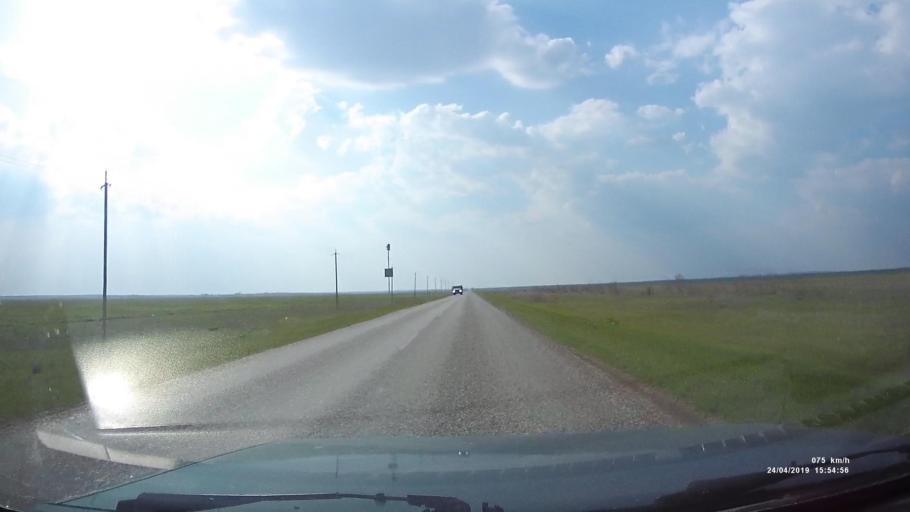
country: RU
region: Kalmykiya
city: Yashalta
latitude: 46.5872
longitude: 42.5586
